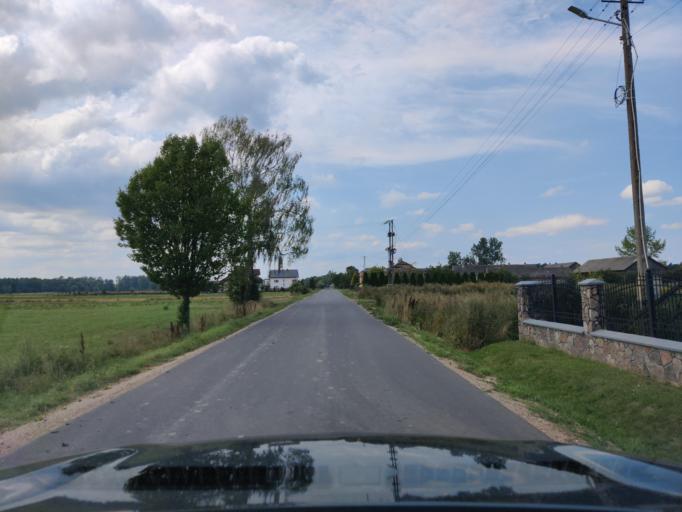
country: PL
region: Masovian Voivodeship
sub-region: Powiat pultuski
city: Obryte
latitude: 52.6892
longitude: 21.2279
